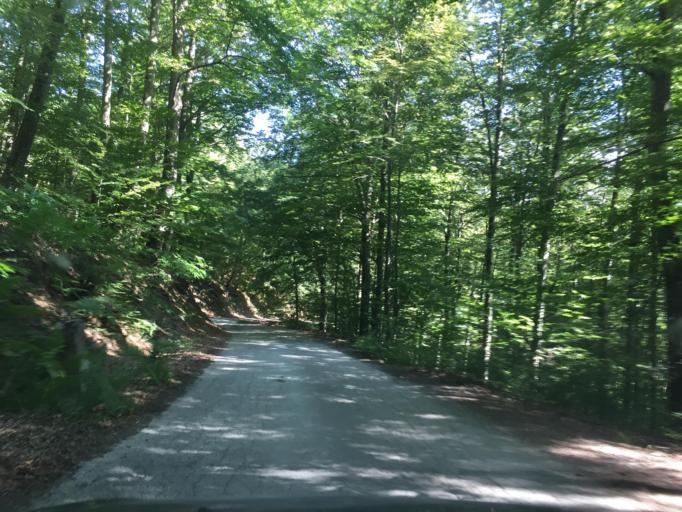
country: HR
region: Primorsko-Goranska
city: Klana
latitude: 45.4721
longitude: 14.3915
